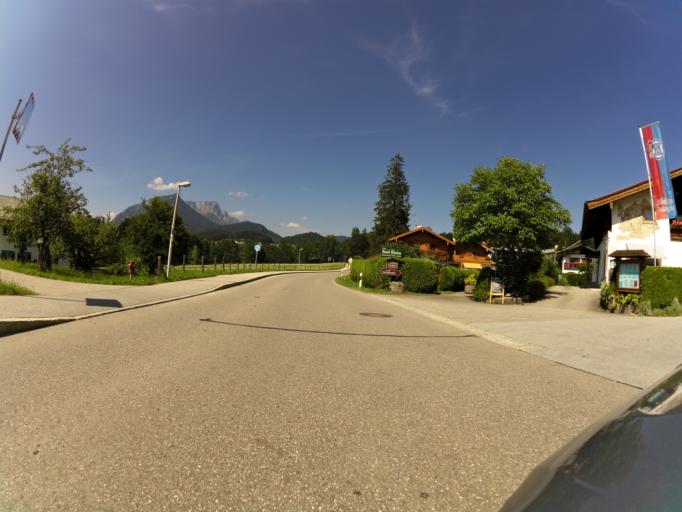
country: DE
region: Bavaria
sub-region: Upper Bavaria
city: Schoenau am Koenigssee
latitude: 47.6177
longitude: 12.9834
